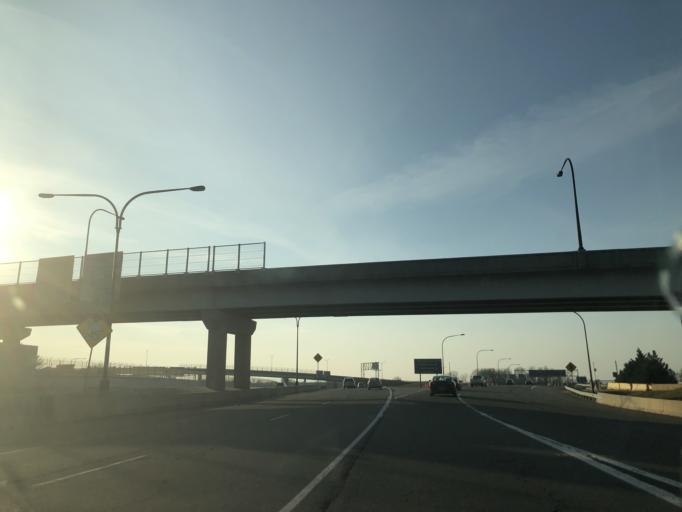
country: US
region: Virginia
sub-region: Fairfax County
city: Floris
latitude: 38.9630
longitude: -77.4386
